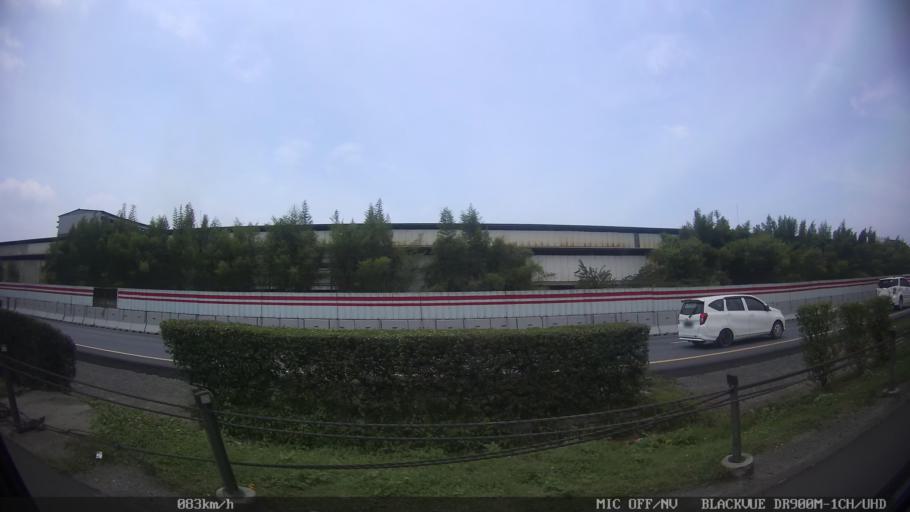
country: ID
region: West Java
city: Kresek
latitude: -6.1667
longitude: 106.3377
